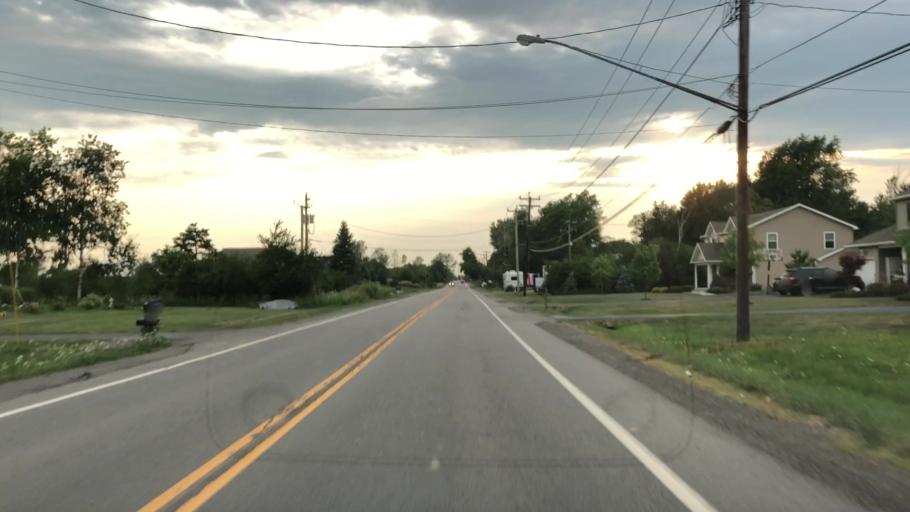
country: US
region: New York
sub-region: Erie County
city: Elma Center
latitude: 42.8390
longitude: -78.6735
